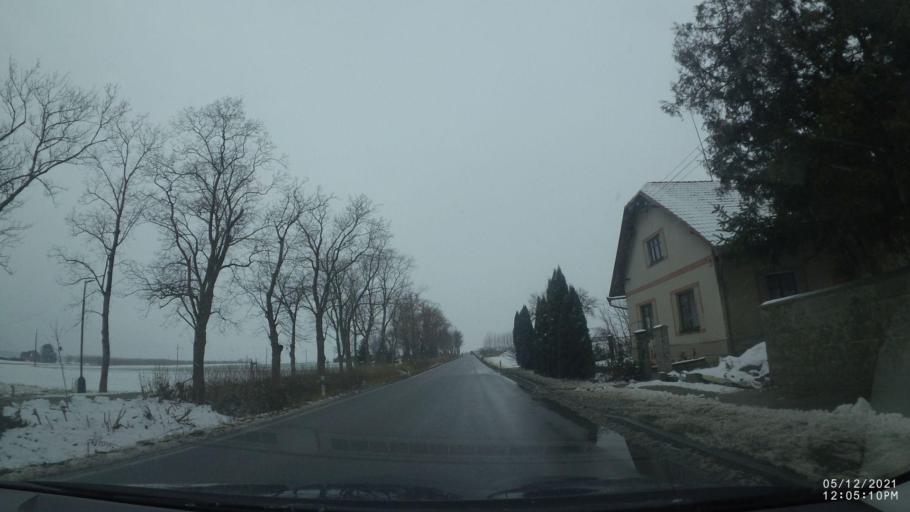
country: CZ
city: Ceske Mezirici
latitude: 50.2866
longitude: 16.0418
